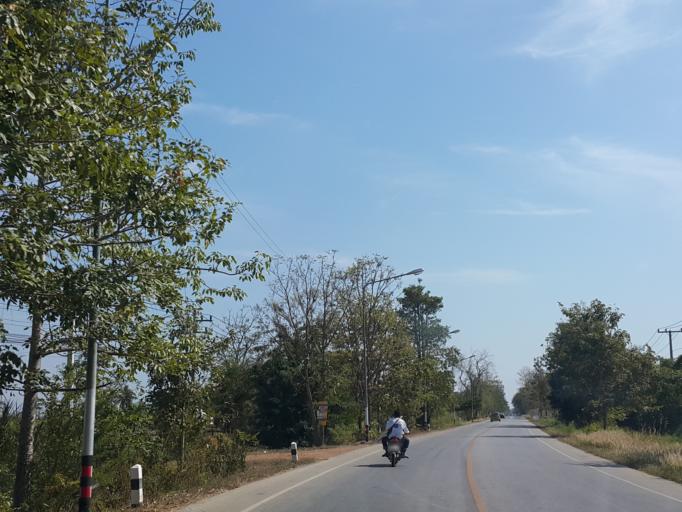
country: TH
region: Sukhothai
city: Thung Saliam
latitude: 17.3178
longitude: 99.6869
